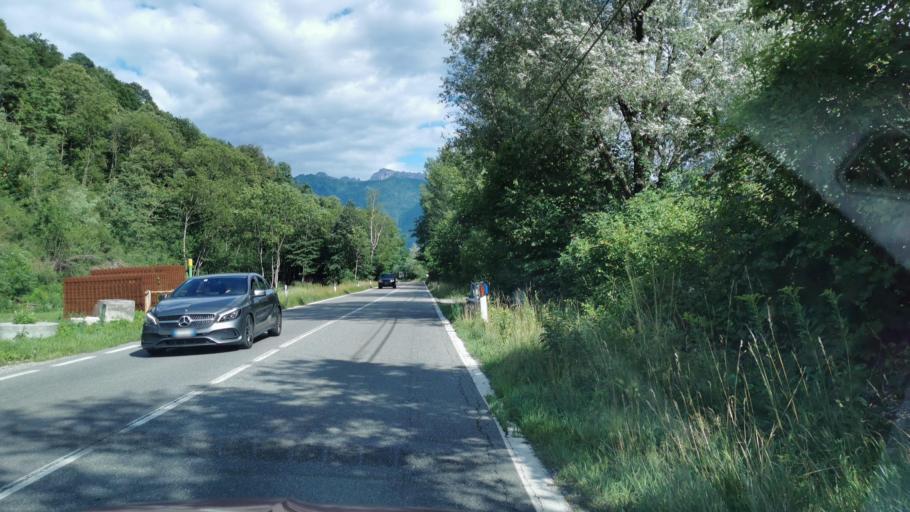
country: IT
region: Lombardy
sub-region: Provincia di Lecco
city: Cortenova
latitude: 45.9947
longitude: 9.4014
